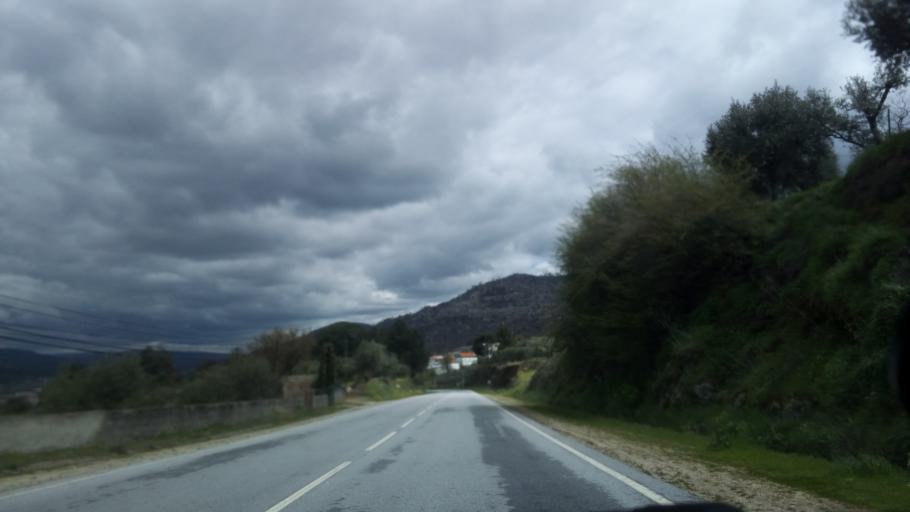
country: PT
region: Guarda
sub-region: Guarda
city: Guarda
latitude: 40.5846
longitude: -7.2919
